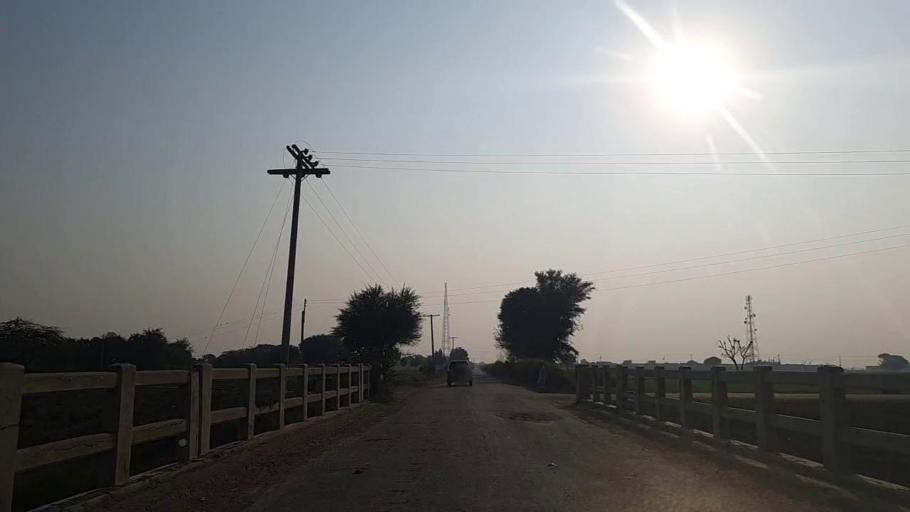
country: PK
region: Sindh
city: Shahpur Chakar
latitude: 26.2027
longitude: 68.5584
